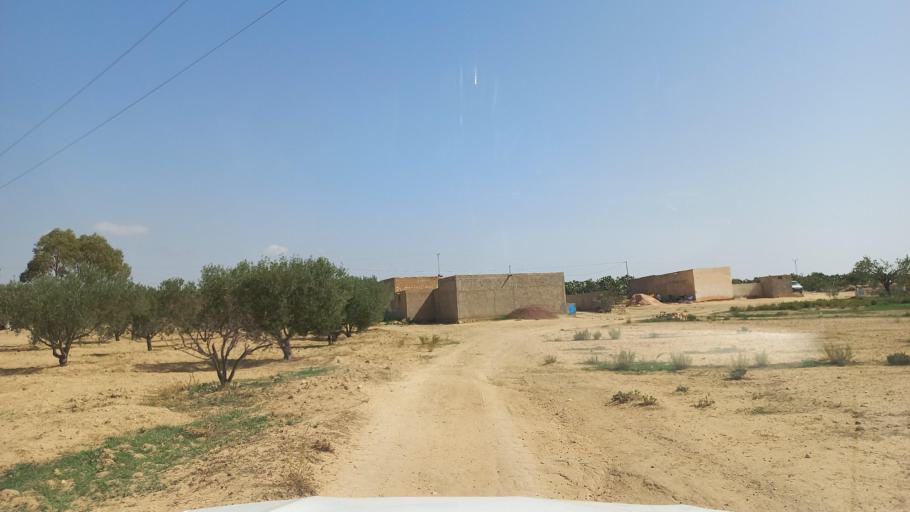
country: TN
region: Al Qasrayn
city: Sbiba
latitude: 35.3927
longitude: 8.9576
